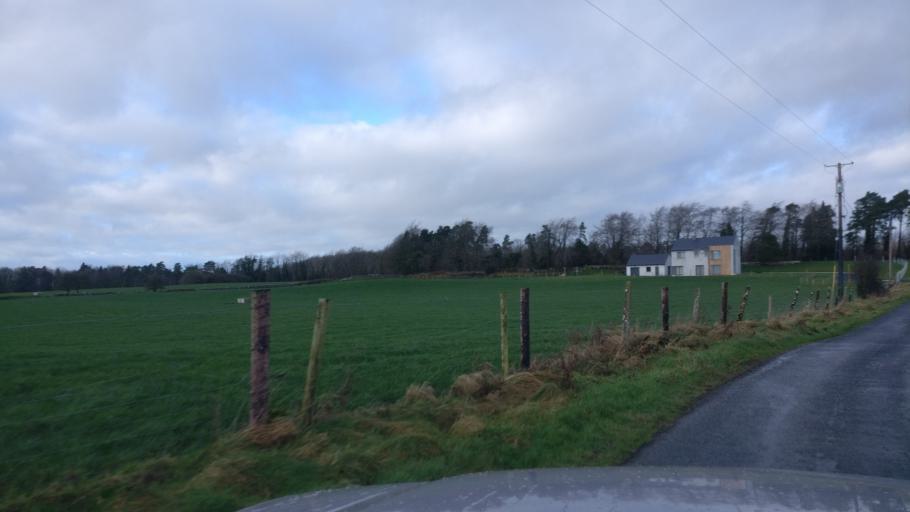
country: IE
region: Connaught
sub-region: County Galway
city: Loughrea
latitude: 53.2414
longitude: -8.6508
